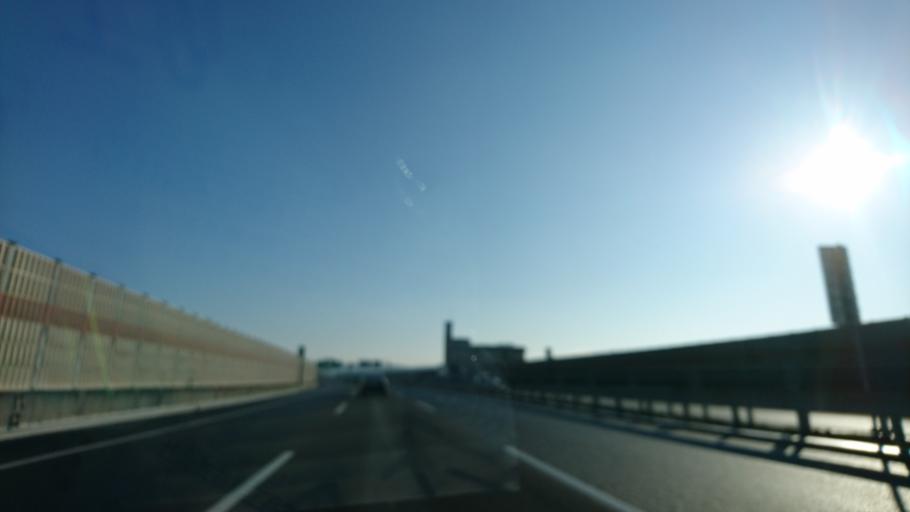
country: JP
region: Okayama
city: Kurashiki
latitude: 34.6248
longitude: 133.7805
